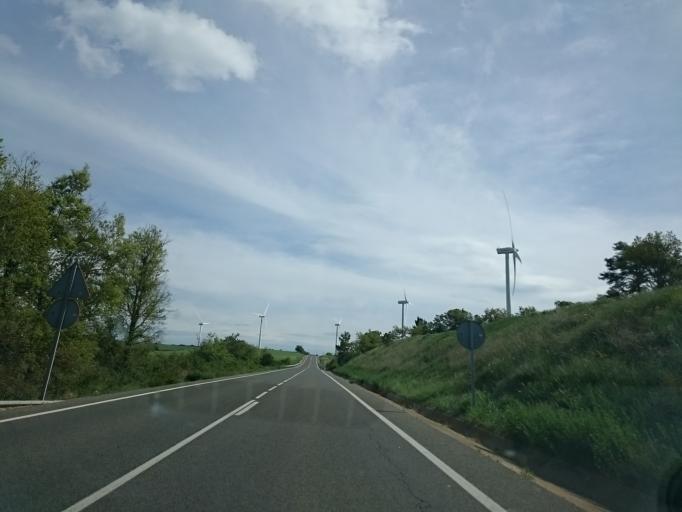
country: ES
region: Catalonia
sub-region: Provincia de Tarragona
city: Santa Coloma de Queralt
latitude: 41.5741
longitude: 1.3938
